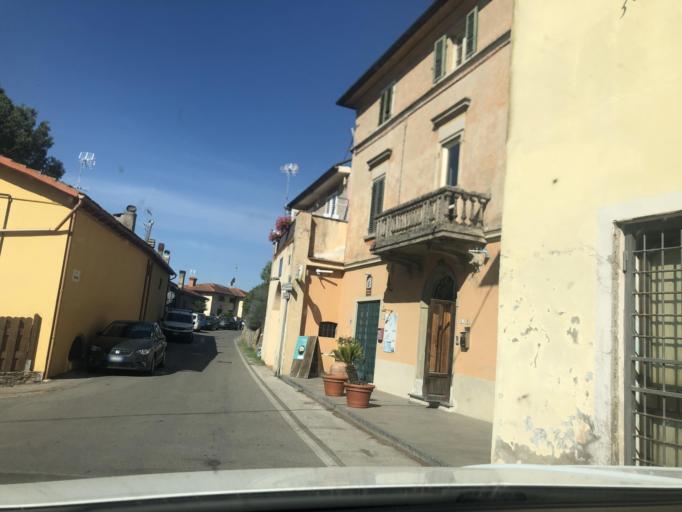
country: IT
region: Tuscany
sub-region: Provincia di Pistoia
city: Larciano
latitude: 43.8394
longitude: 10.9170
